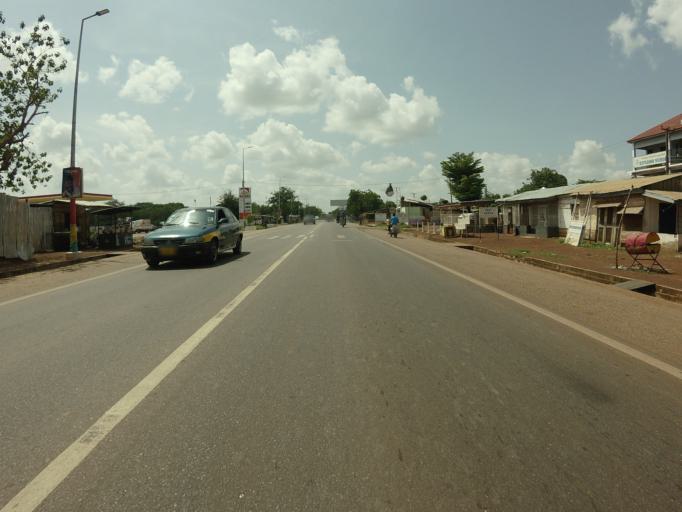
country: GH
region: Northern
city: Tamale
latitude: 9.4515
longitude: -0.8450
